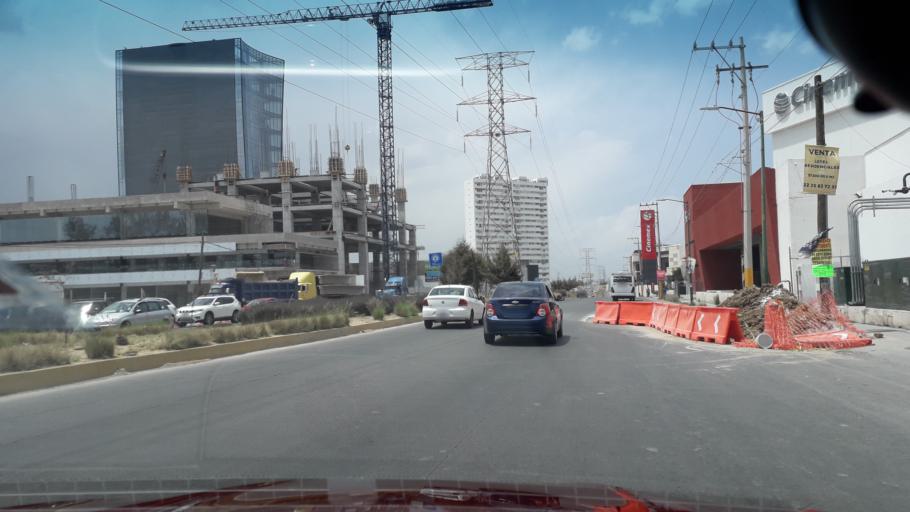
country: MX
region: Puebla
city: Tlazcalancingo
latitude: 19.0087
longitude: -98.2444
